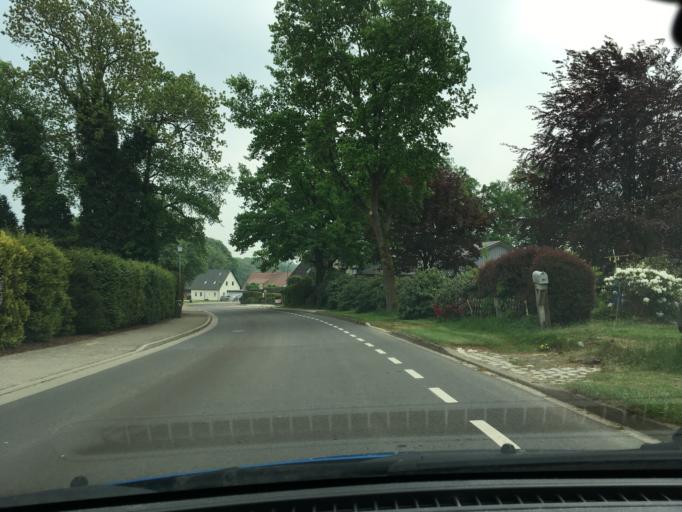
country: DE
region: Lower Saxony
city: Seevetal
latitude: 53.4085
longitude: 9.8966
